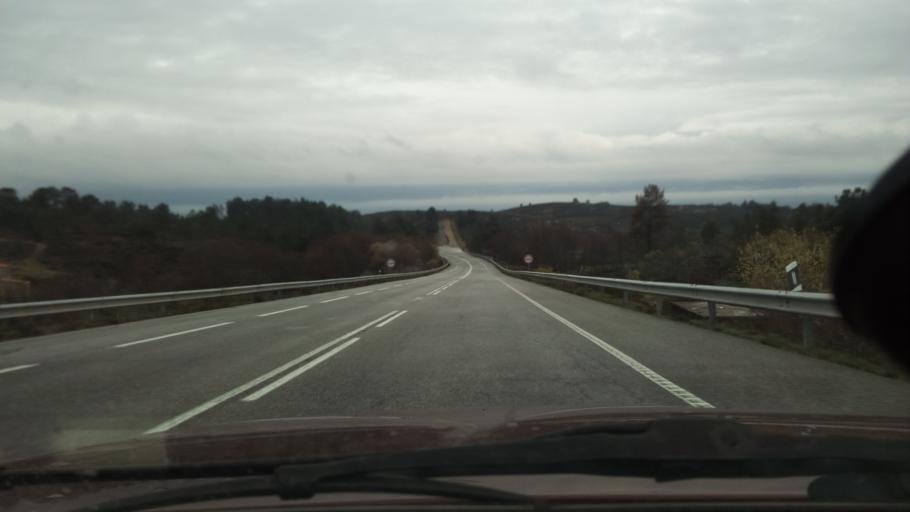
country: PT
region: Guarda
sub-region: Fornos de Algodres
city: Fornos de Algodres
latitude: 40.6083
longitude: -7.5902
